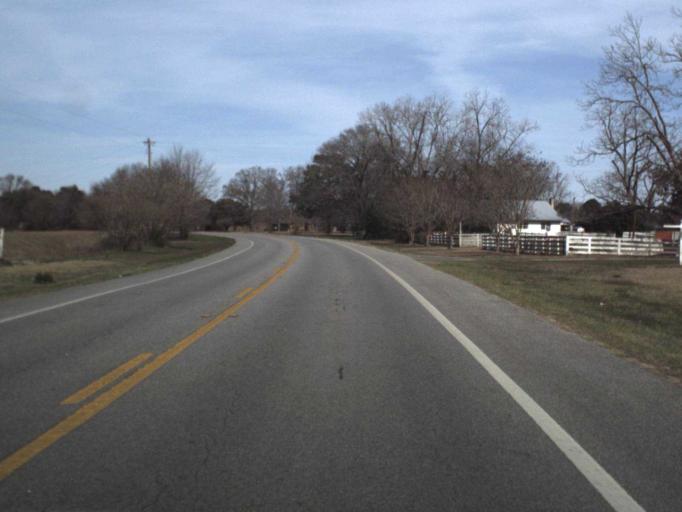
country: US
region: Florida
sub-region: Jackson County
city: Graceville
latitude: 30.9868
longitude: -85.4821
